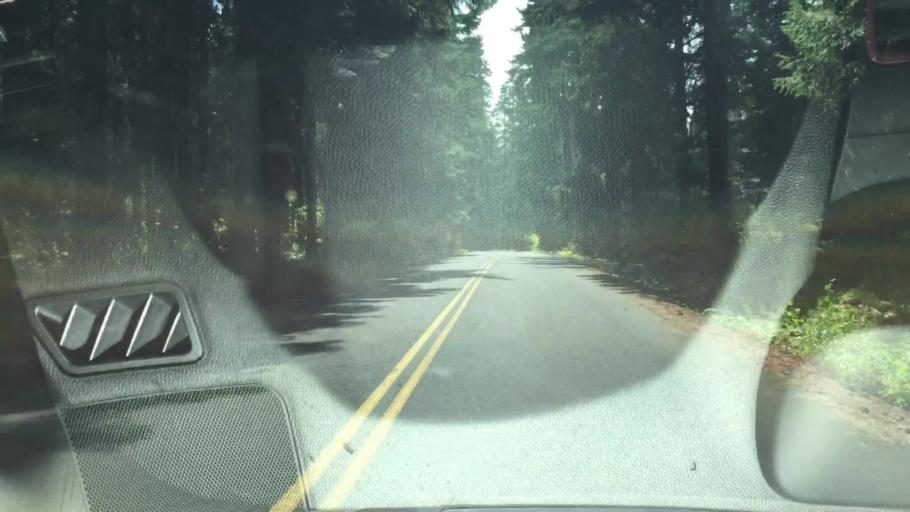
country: US
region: Washington
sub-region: Klickitat County
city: White Salmon
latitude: 46.0472
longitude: -121.5565
